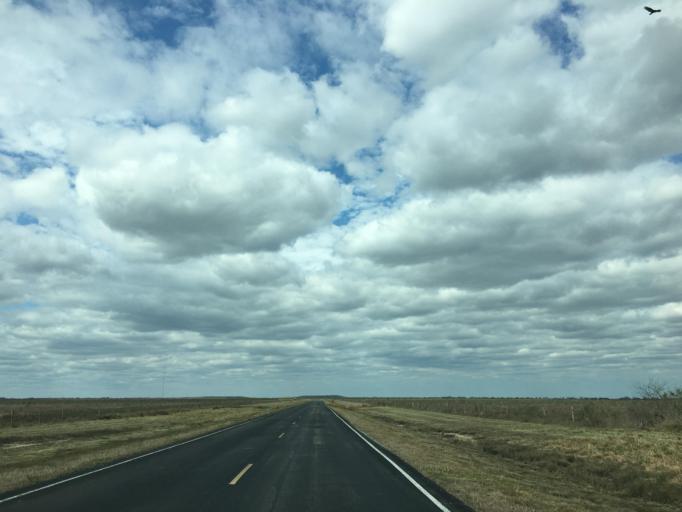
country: US
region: Texas
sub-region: Brazoria County
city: Oyster Creek
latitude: 29.0632
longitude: -95.2886
